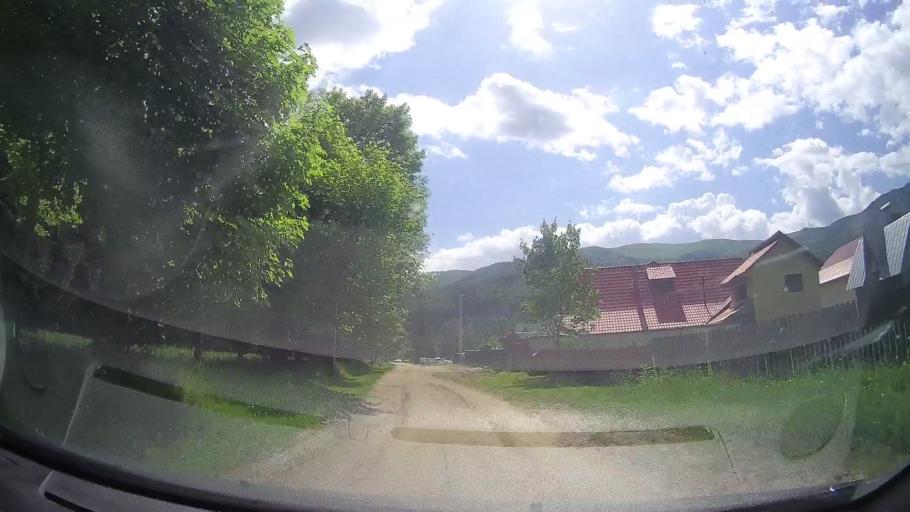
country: RO
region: Brasov
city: Crivina
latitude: 45.4569
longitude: 25.9413
